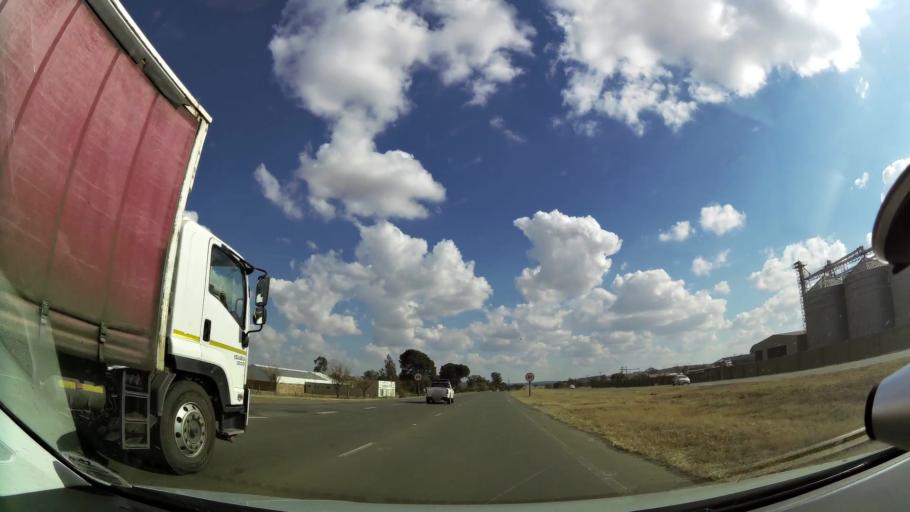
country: ZA
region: Orange Free State
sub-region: Mangaung Metropolitan Municipality
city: Bloemfontein
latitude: -29.1325
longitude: 26.1446
